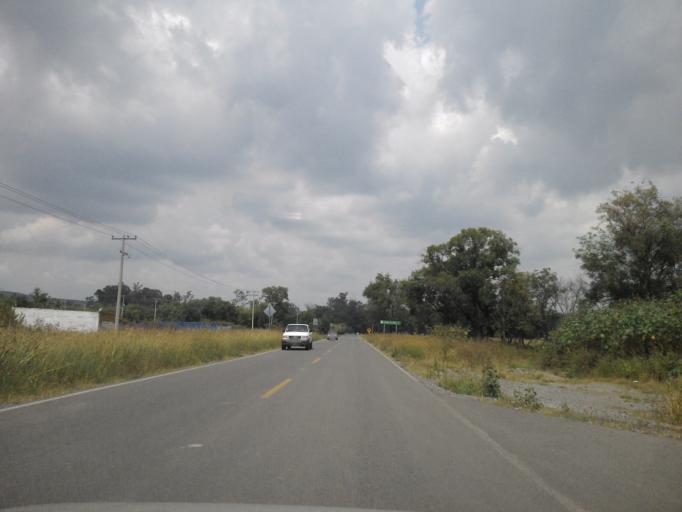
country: MX
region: Jalisco
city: San Diego de Alejandria
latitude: 20.8718
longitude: -101.9868
